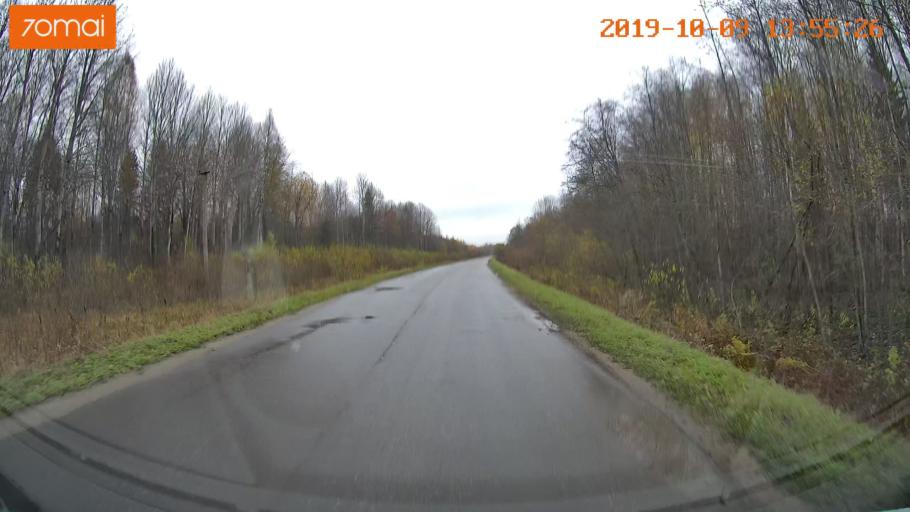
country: RU
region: Kostroma
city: Buy
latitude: 58.4244
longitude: 41.2736
